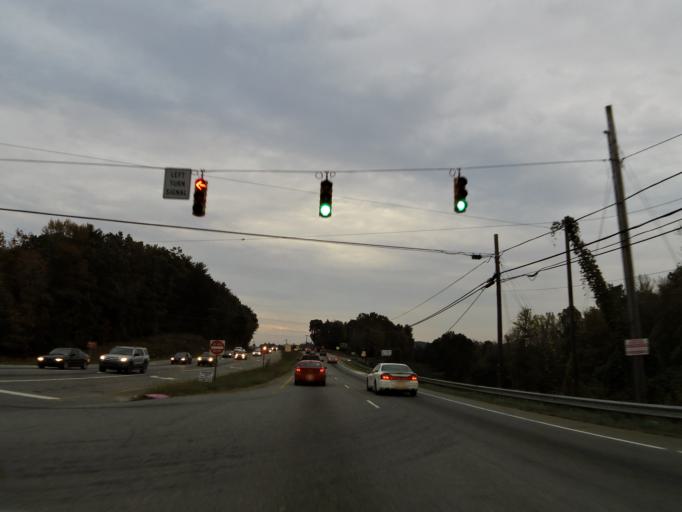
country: US
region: North Carolina
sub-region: Caldwell County
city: Northlakes
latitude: 35.7630
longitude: -81.3828
